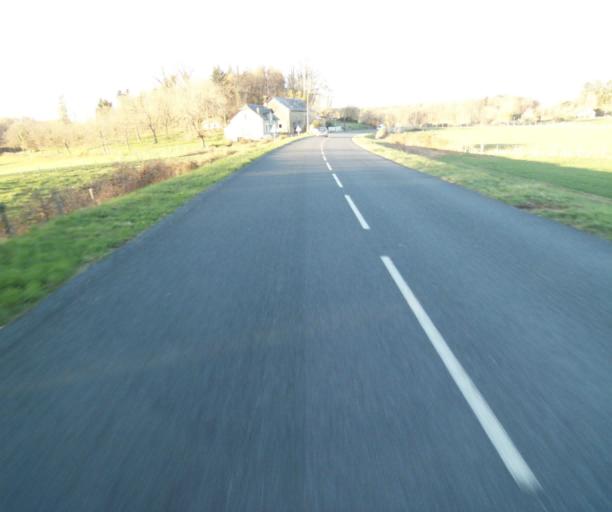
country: FR
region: Limousin
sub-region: Departement de la Correze
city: Saint-Clement
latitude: 45.3503
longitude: 1.7016
